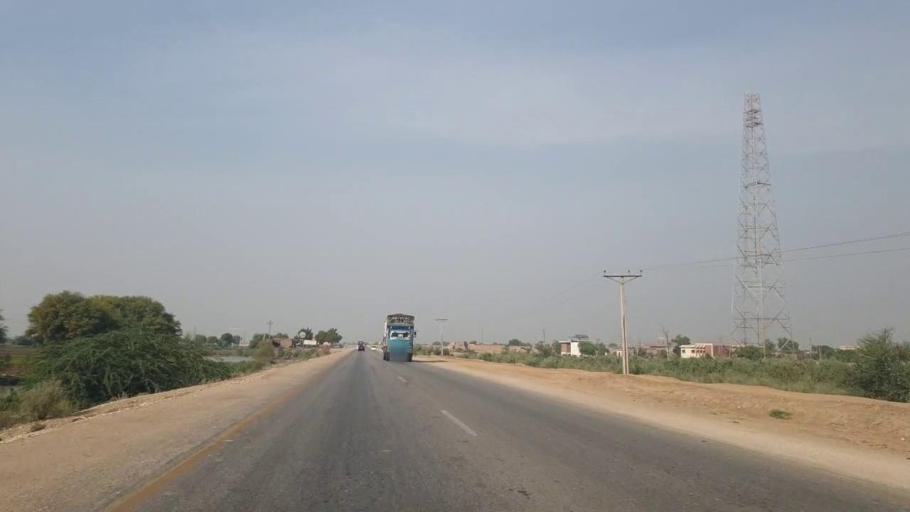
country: PK
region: Sindh
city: Sann
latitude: 26.0860
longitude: 68.0921
